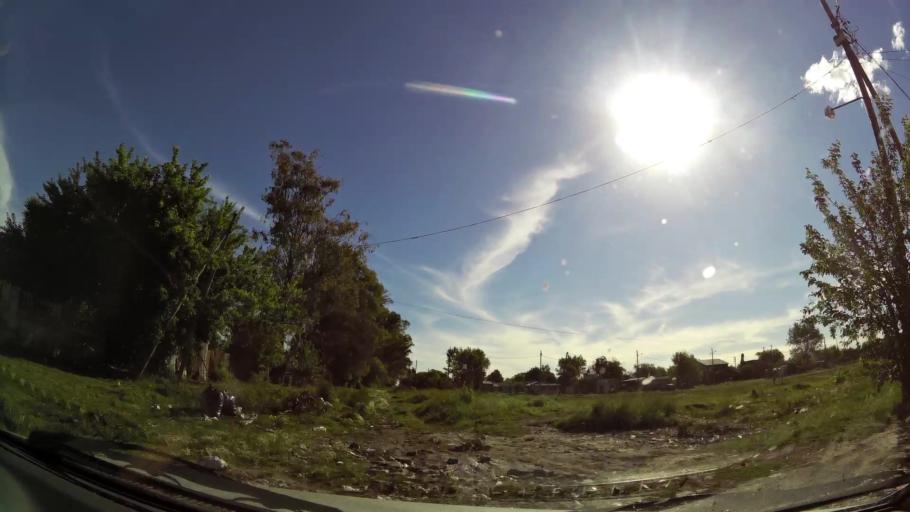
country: AR
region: Buenos Aires
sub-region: Partido de Almirante Brown
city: Adrogue
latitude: -34.8255
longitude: -58.3437
